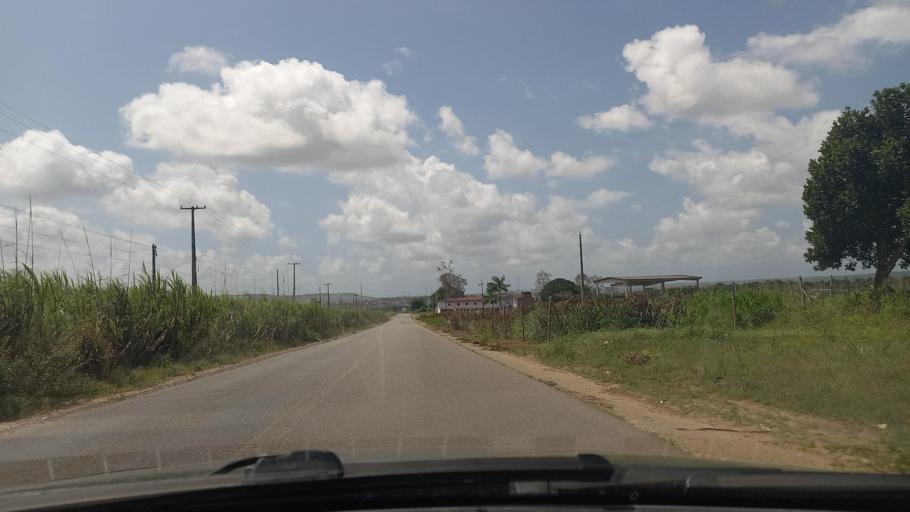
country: BR
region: Pernambuco
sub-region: Goiana
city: Goiana
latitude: -7.5579
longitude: -35.0301
